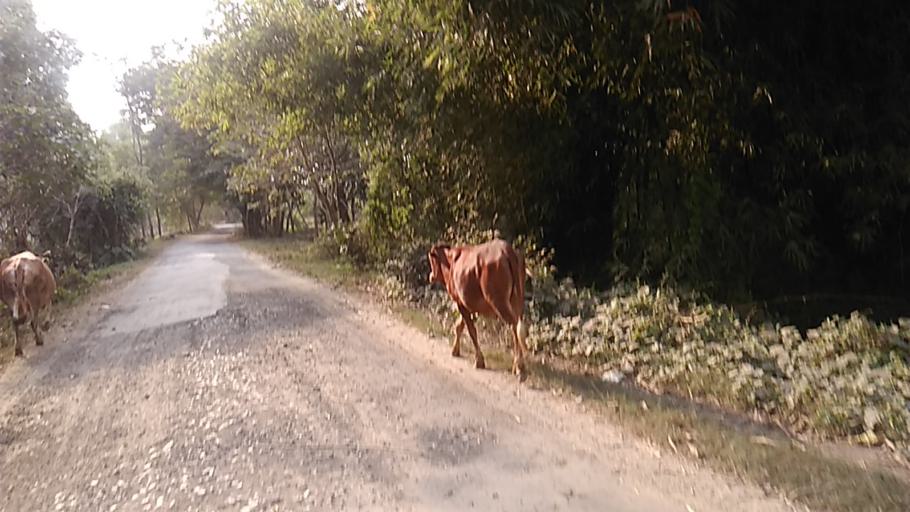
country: IN
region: West Bengal
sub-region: Nadia
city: Navadwip
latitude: 23.4283
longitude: 88.4024
